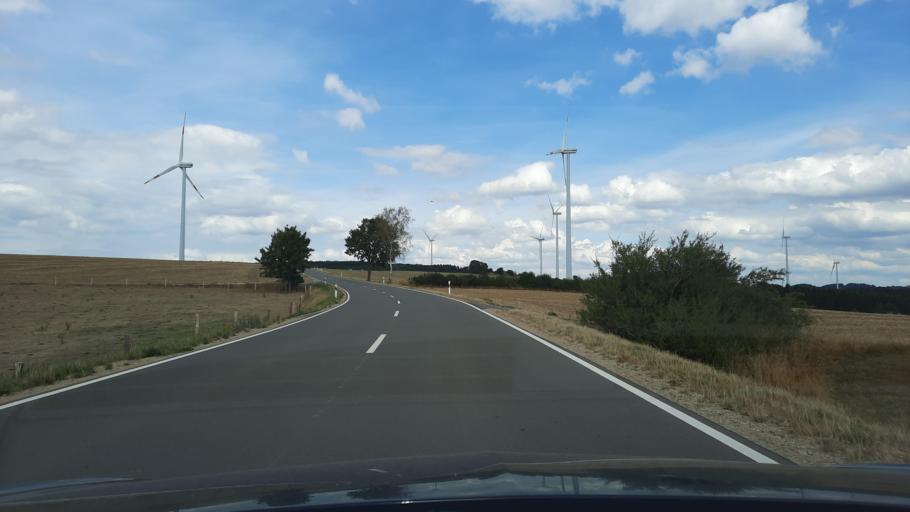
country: DE
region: Rheinland-Pfalz
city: Pronsfeld
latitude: 50.1822
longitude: 6.3263
